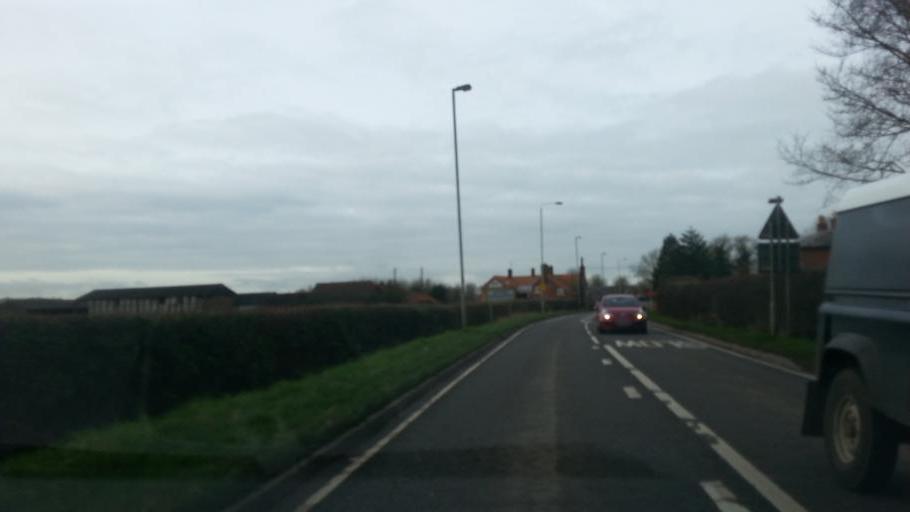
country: GB
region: England
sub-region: Leicestershire
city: Grimston
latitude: 52.8227
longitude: -0.9632
